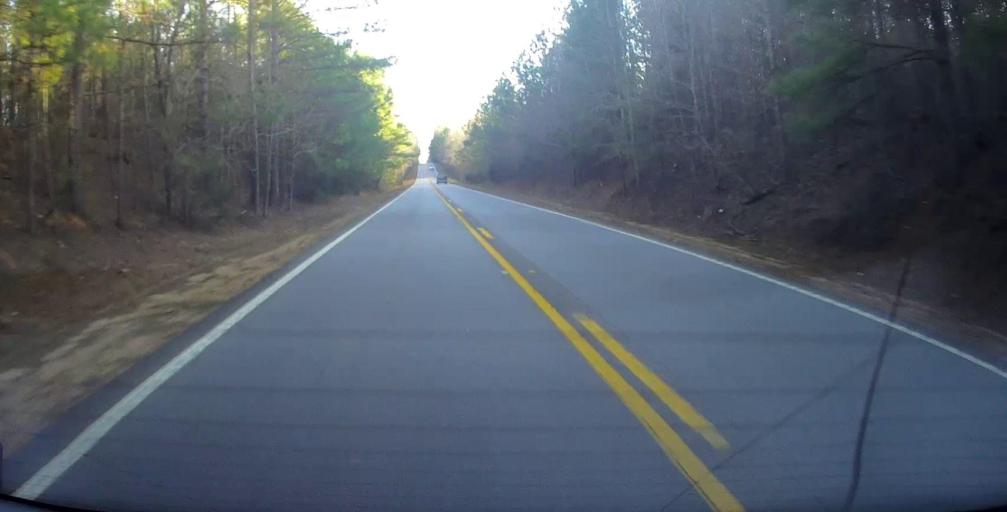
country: US
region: Alabama
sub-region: Chambers County
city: Valley
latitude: 32.8120
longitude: -85.1036
